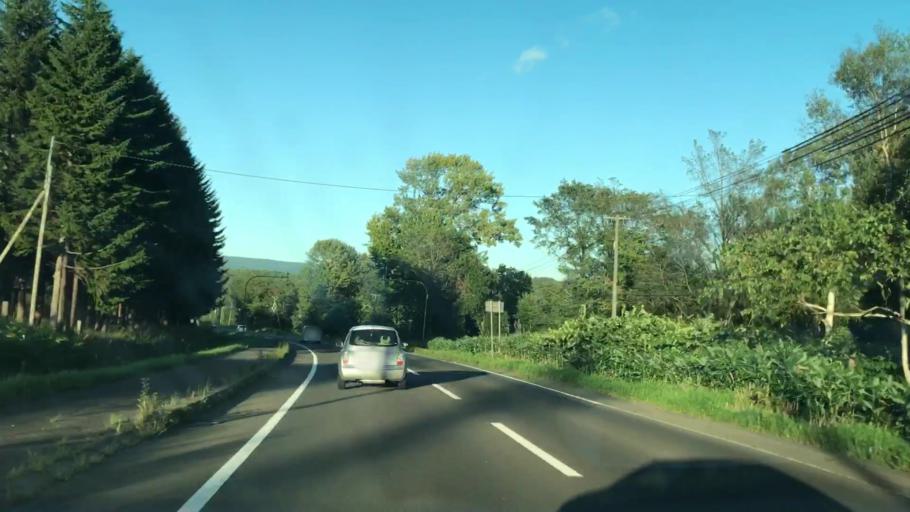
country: JP
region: Hokkaido
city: Niseko Town
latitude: 42.7537
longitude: 140.9181
